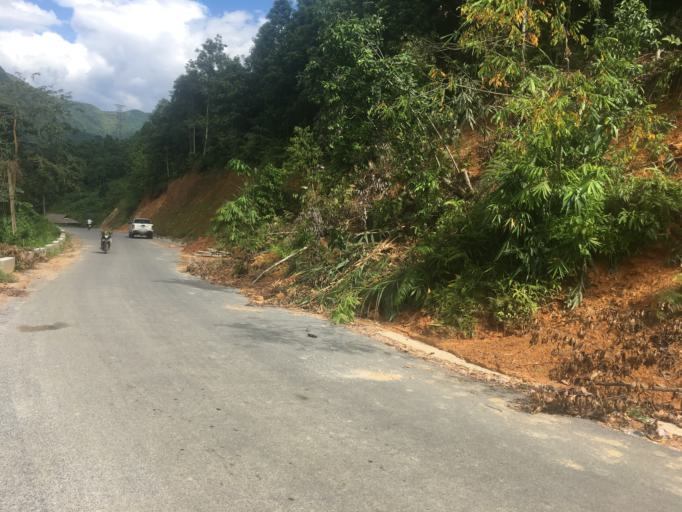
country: VN
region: Ha Giang
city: Thanh Pho Ha Giang
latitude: 22.8567
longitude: 105.0390
